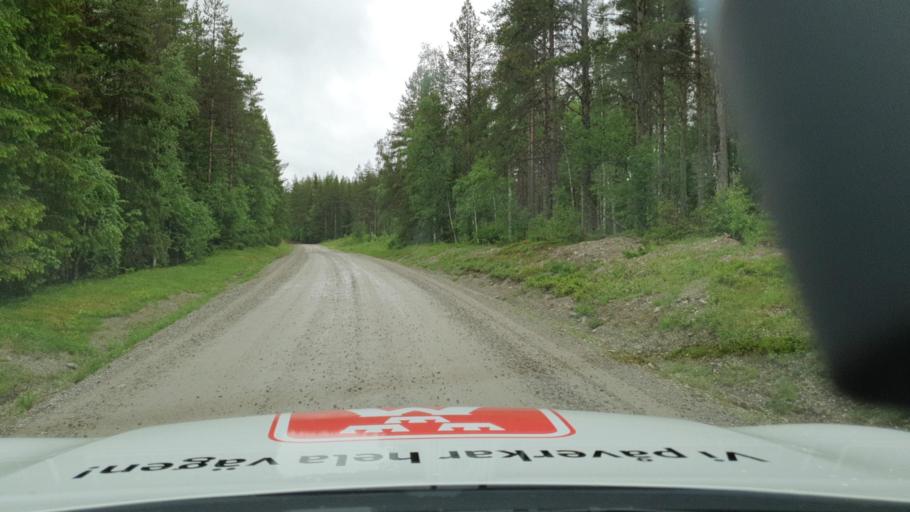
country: SE
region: Vaesterbotten
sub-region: Dorotea Kommun
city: Dorotea
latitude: 64.0305
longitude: 16.7713
